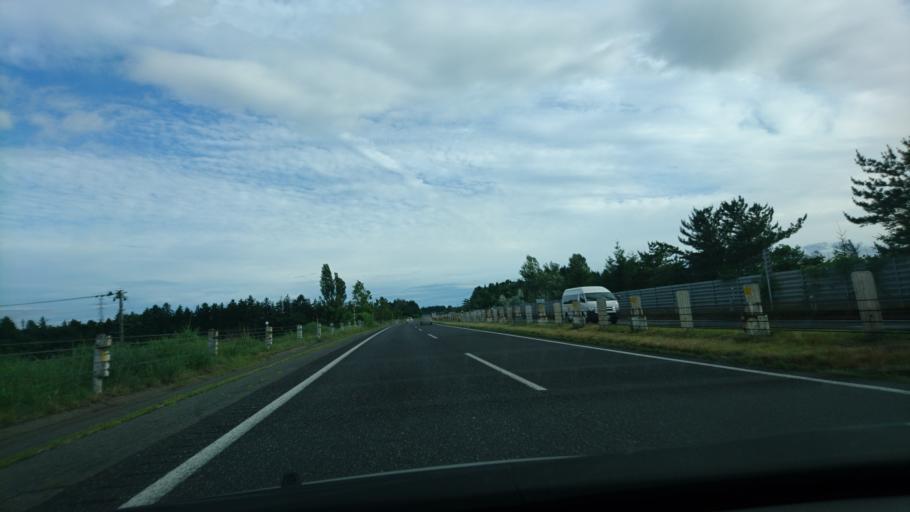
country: JP
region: Iwate
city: Hanamaki
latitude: 39.3401
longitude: 141.0915
